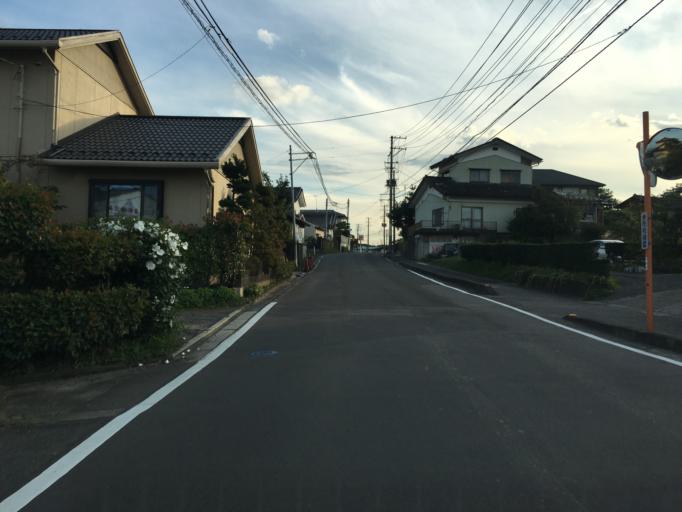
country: JP
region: Fukushima
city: Hobaramachi
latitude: 37.8283
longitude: 140.5051
